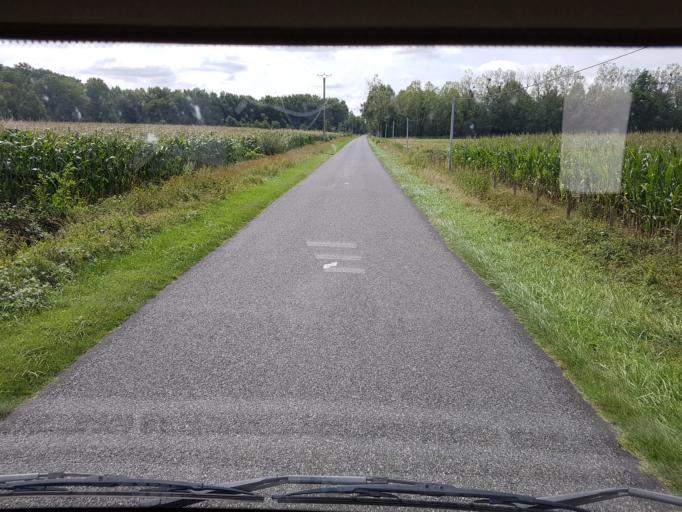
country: FR
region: Rhone-Alpes
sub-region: Departement de l'Ain
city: Villars-les-Dombes
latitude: 45.9546
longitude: 5.0896
